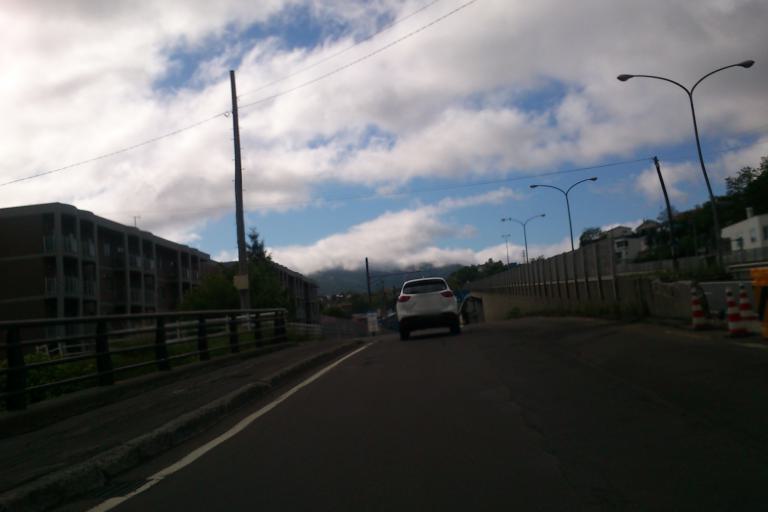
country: JP
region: Hokkaido
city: Otaru
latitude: 43.1828
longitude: 141.0181
